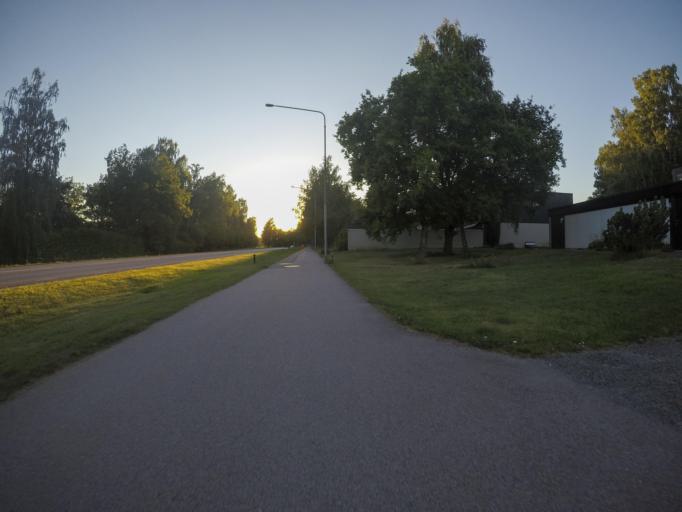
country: SE
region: Vaestmanland
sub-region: Vasteras
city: Vasteras
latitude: 59.6029
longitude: 16.5979
